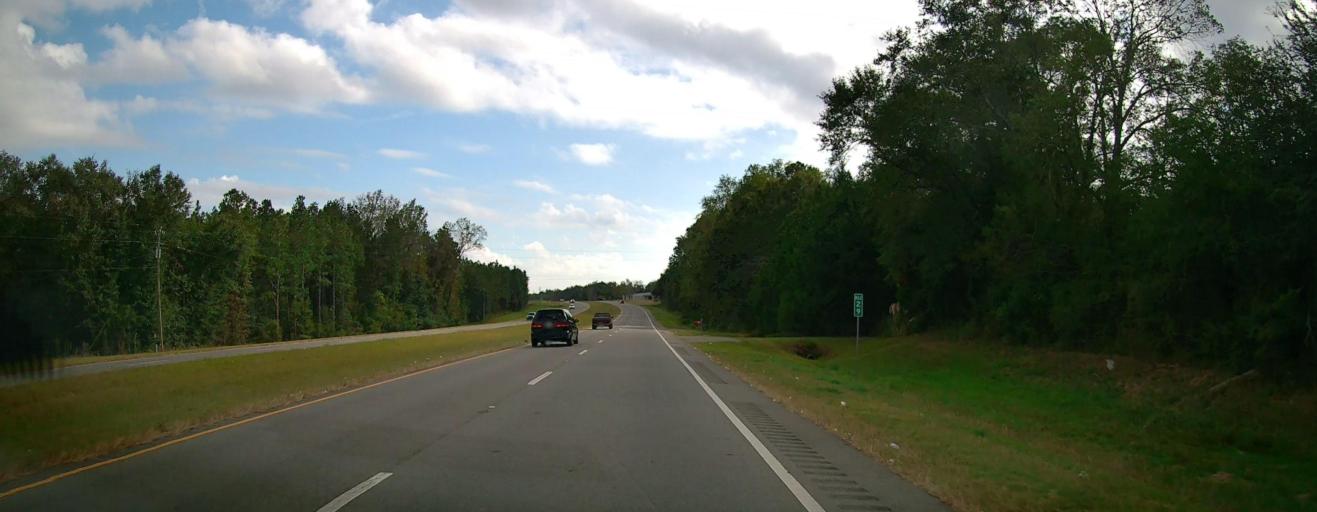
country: US
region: Georgia
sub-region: Thomas County
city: Meigs
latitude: 31.0507
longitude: -84.0710
